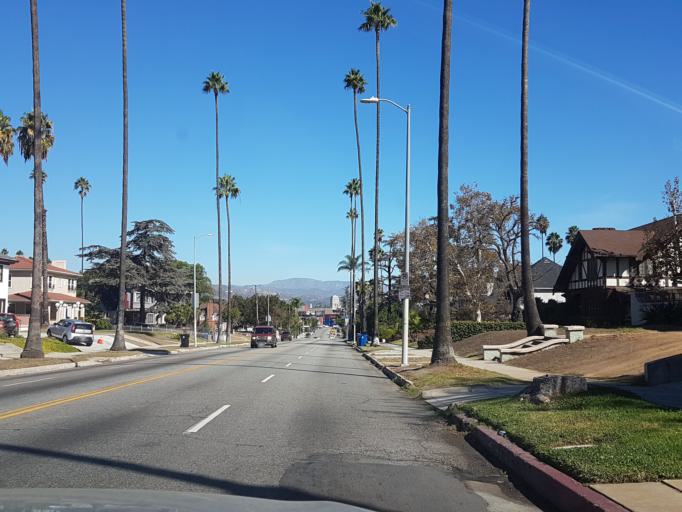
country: US
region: California
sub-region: Los Angeles County
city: Hollywood
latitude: 34.0476
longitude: -118.3174
